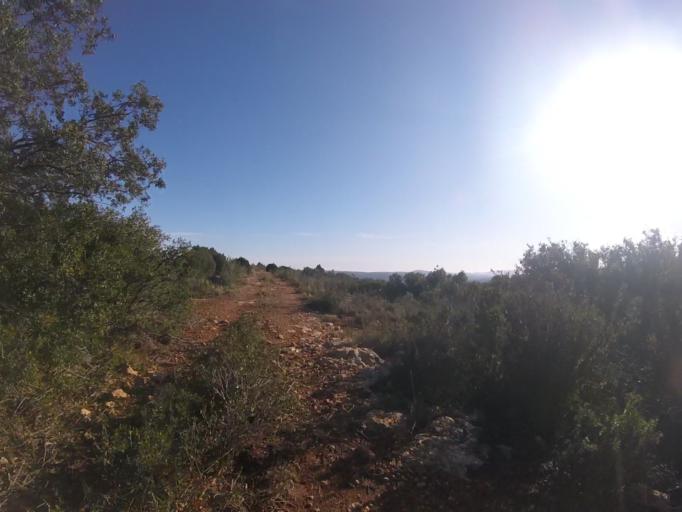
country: ES
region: Valencia
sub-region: Provincia de Castello
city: Sarratella
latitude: 40.2901
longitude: 0.0541
